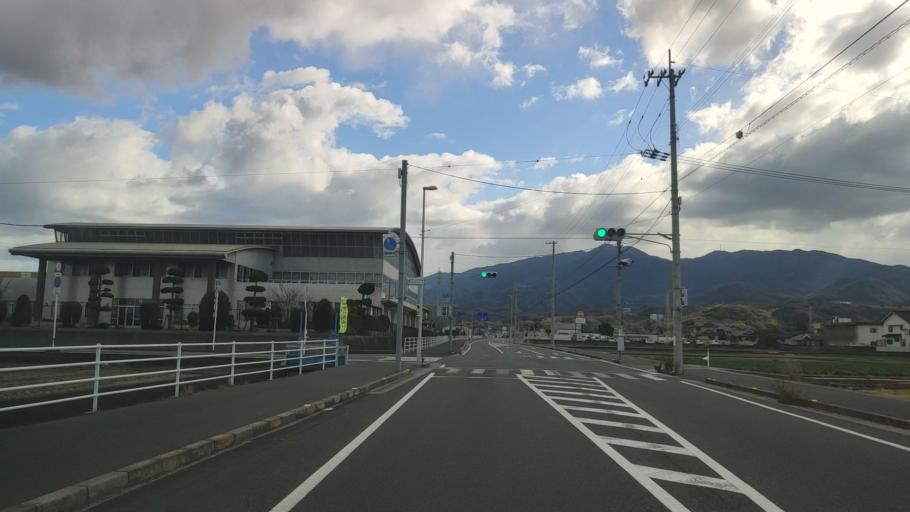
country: JP
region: Ehime
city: Hojo
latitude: 33.9705
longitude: 132.7796
